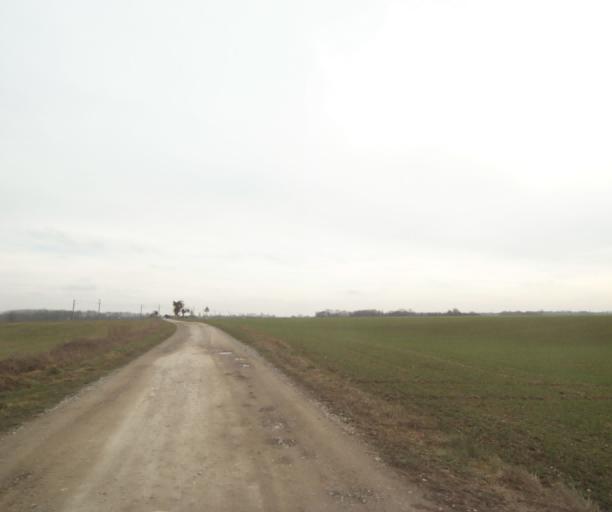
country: FR
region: Champagne-Ardenne
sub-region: Departement de la Haute-Marne
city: Villiers-en-Lieu
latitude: 48.6739
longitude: 4.8747
